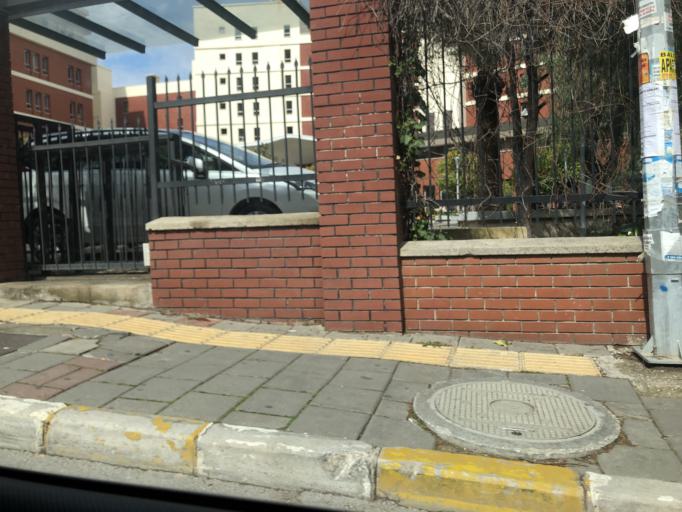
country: TR
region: Izmir
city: Karabaglar
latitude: 38.3878
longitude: 27.0450
